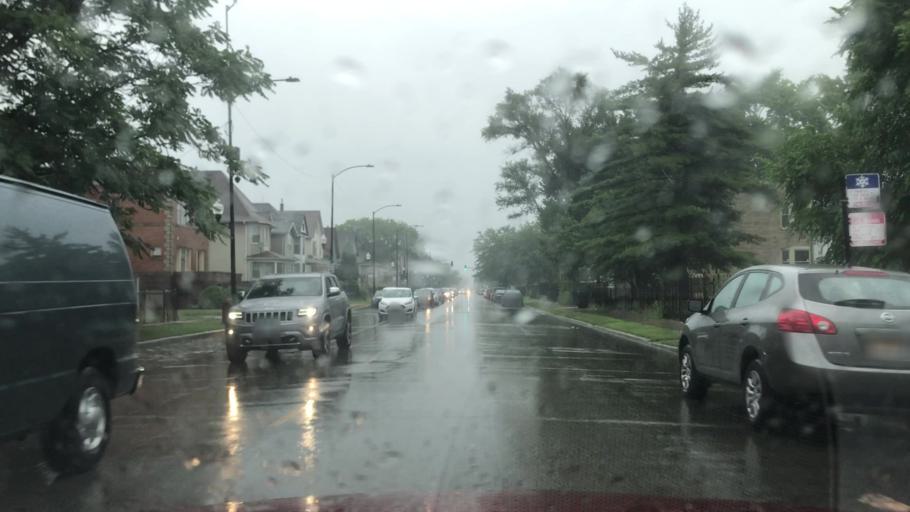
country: US
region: Illinois
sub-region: Cook County
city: Oak Park
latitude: 41.8896
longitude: -87.7554
